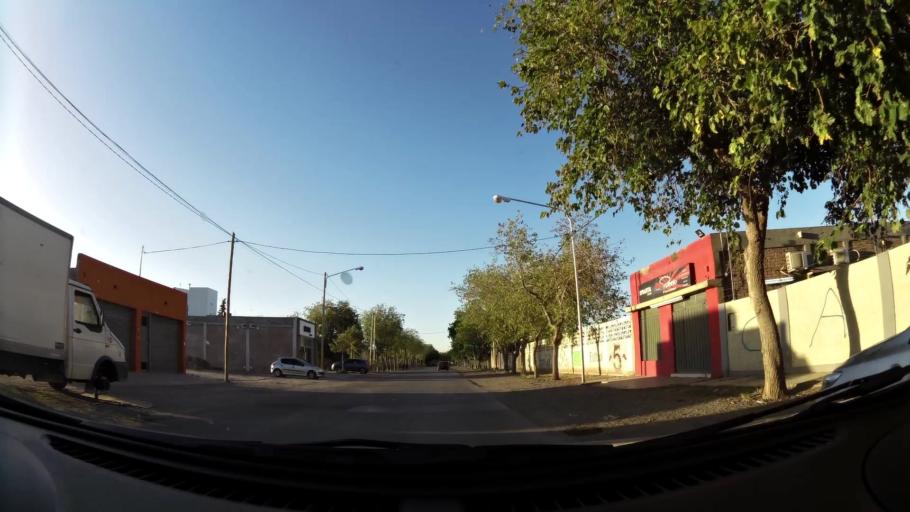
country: AR
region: San Juan
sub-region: Departamento de Santa Lucia
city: Santa Lucia
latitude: -31.5360
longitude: -68.4937
